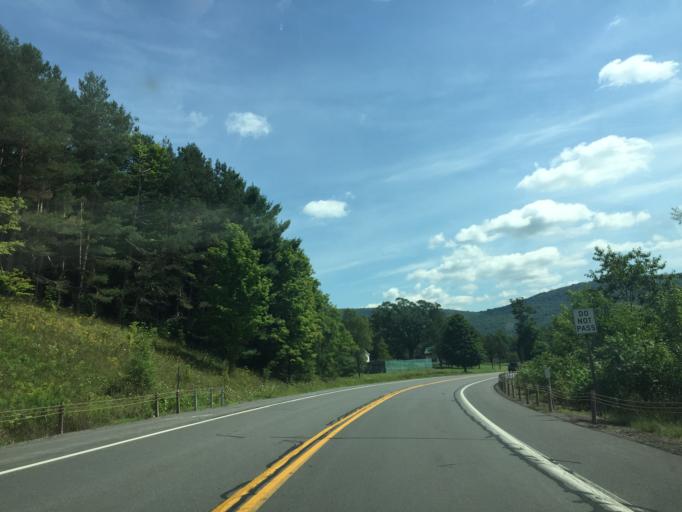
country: US
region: New York
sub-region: Delaware County
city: Delhi
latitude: 42.3012
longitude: -74.8975
